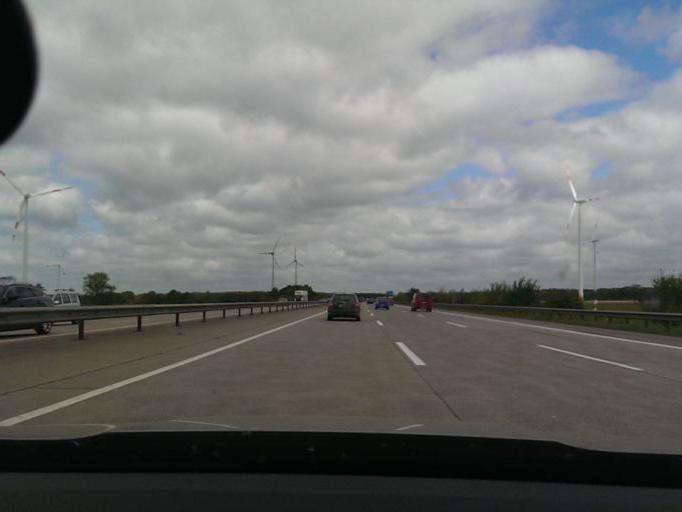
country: DE
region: Lower Saxony
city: Lindwedel
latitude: 52.6450
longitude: 9.7103
